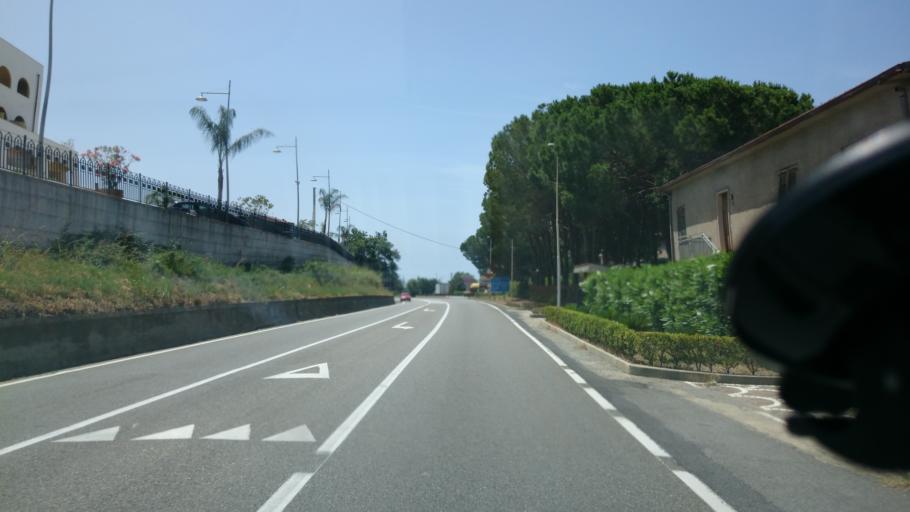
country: IT
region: Calabria
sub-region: Provincia di Cosenza
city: Cittadella del Capo
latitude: 39.5805
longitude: 15.8696
